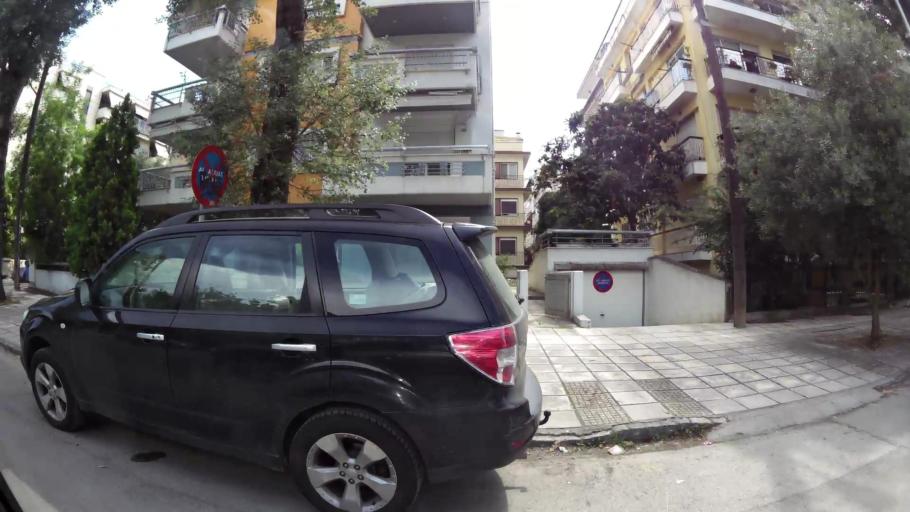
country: GR
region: Central Macedonia
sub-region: Nomos Thessalonikis
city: Kalamaria
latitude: 40.5923
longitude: 22.9509
